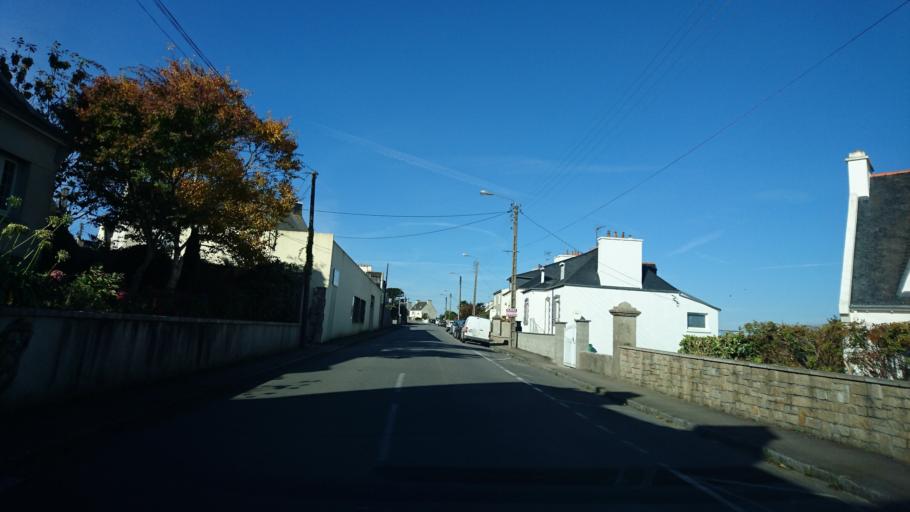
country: FR
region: Brittany
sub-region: Departement du Finistere
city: Saint-Renan
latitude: 48.4321
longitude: -4.6263
